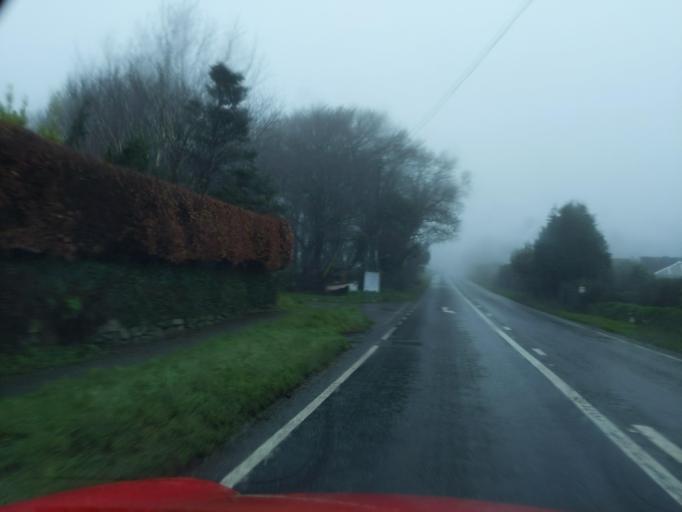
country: GB
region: England
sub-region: Cornwall
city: Callington
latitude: 50.5213
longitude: -4.3173
